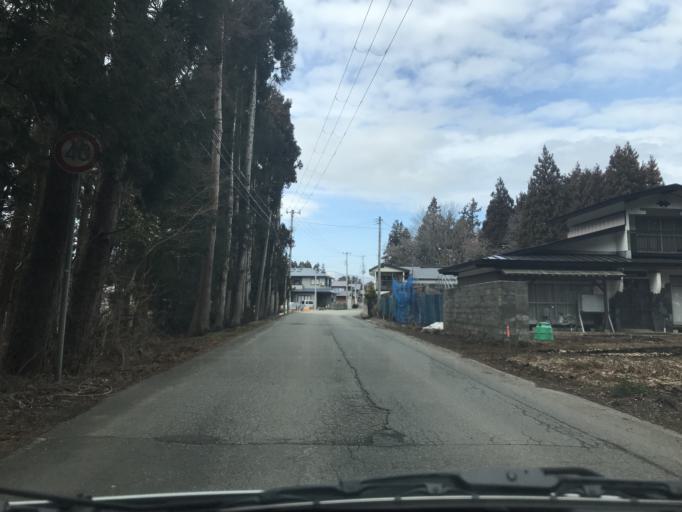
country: JP
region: Iwate
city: Hanamaki
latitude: 39.3345
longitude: 140.9837
